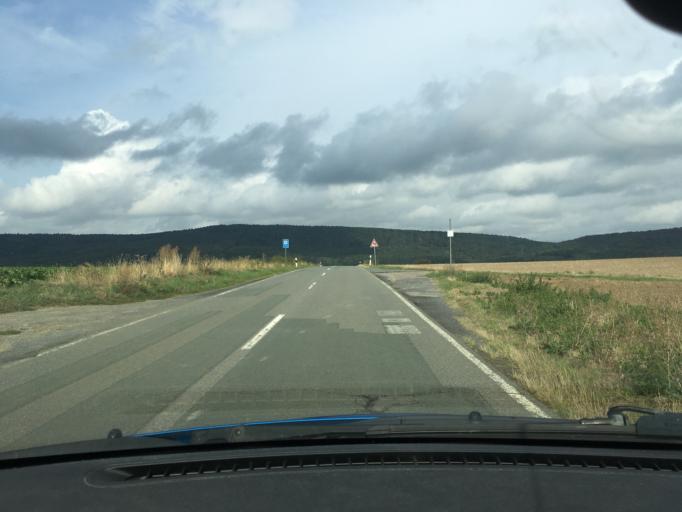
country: DE
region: Lower Saxony
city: Barsinghausen
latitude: 52.2486
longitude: 9.4411
